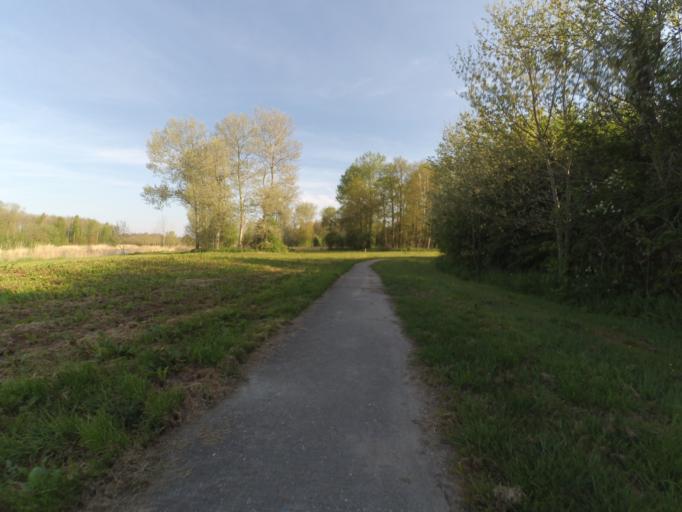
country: NL
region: North Holland
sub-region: Gemeente Huizen
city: Huizen
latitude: 52.3335
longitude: 5.2969
